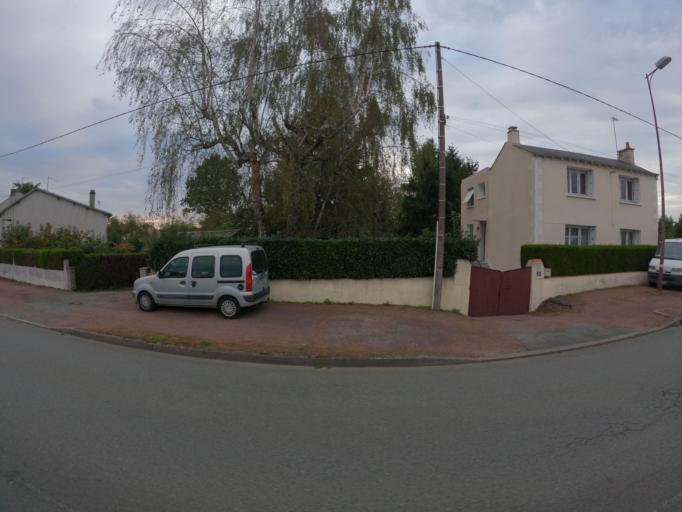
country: FR
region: Poitou-Charentes
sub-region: Departement des Deux-Sevres
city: Parthenay
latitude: 46.6597
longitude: -0.2479
